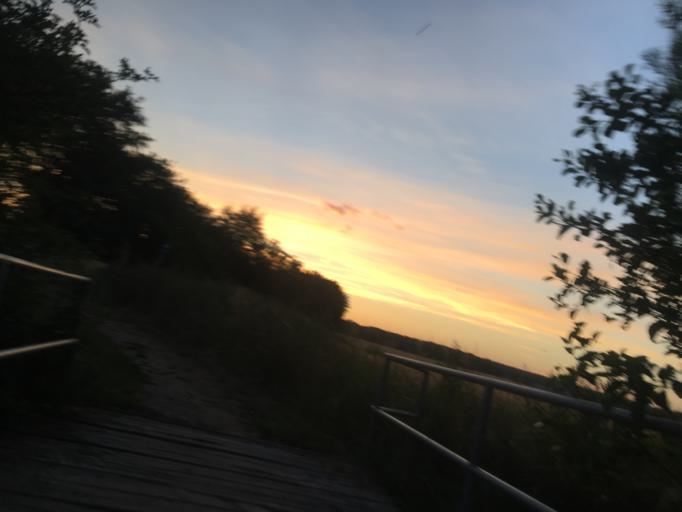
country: DK
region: Central Jutland
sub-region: Syddjurs Kommune
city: Hornslet
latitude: 56.3214
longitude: 10.3345
